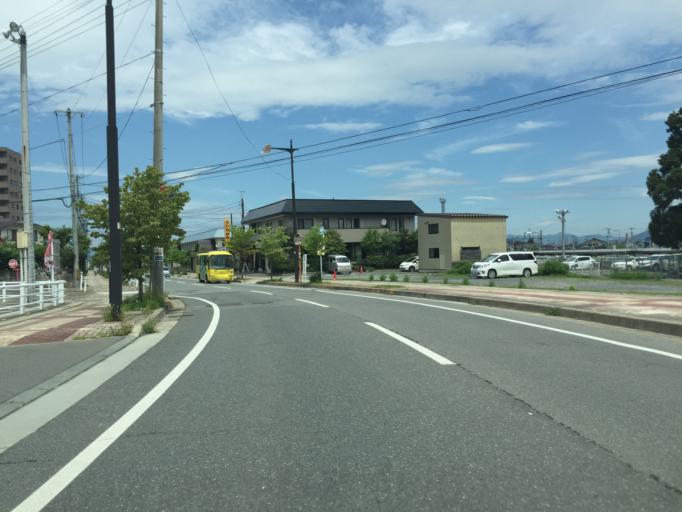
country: JP
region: Yamagata
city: Yonezawa
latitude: 37.9071
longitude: 140.1282
